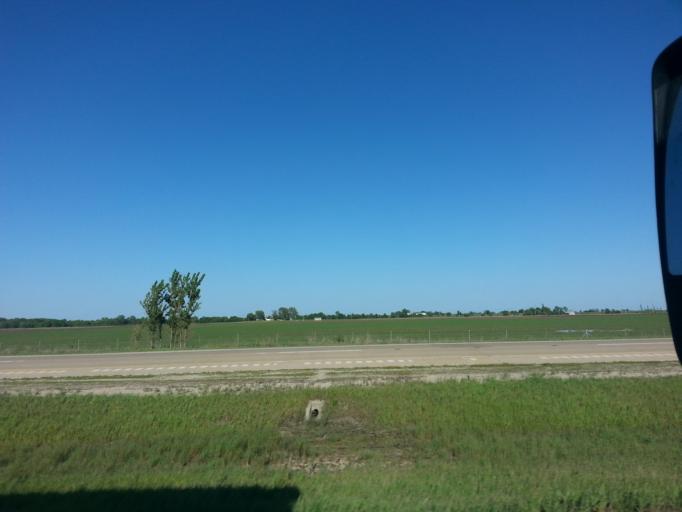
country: US
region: Illinois
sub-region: Woodford County
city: Minonk
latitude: 40.9723
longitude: -89.0565
